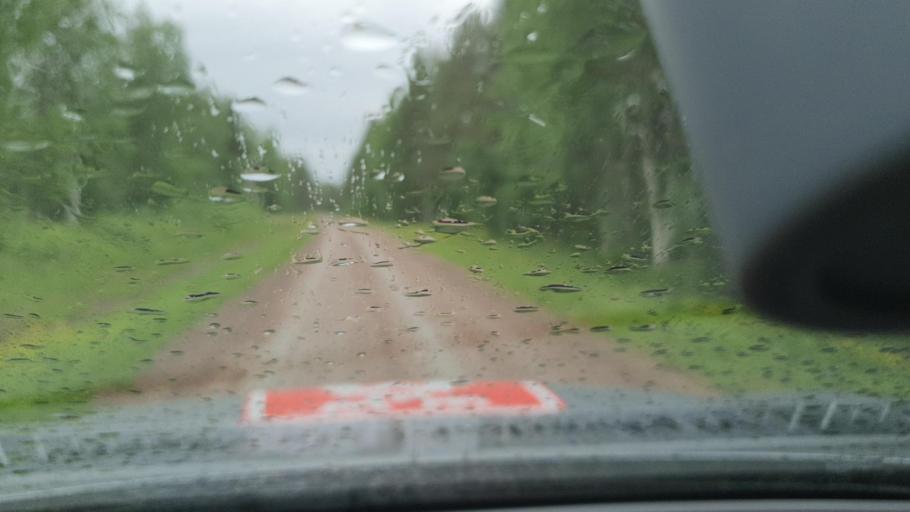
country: SE
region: Norrbotten
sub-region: Overkalix Kommun
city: OEverkalix
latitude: 66.5523
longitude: 22.7460
